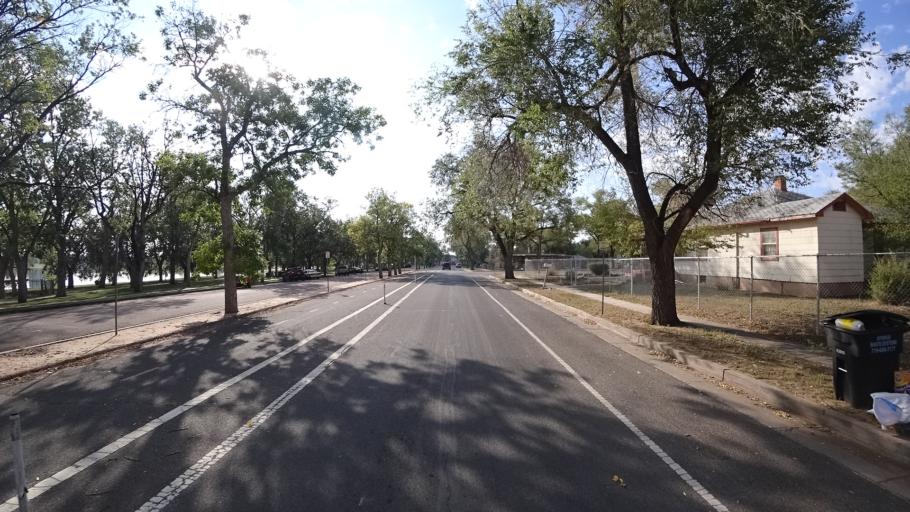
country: US
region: Colorado
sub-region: El Paso County
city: Colorado Springs
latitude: 38.8243
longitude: -104.8014
